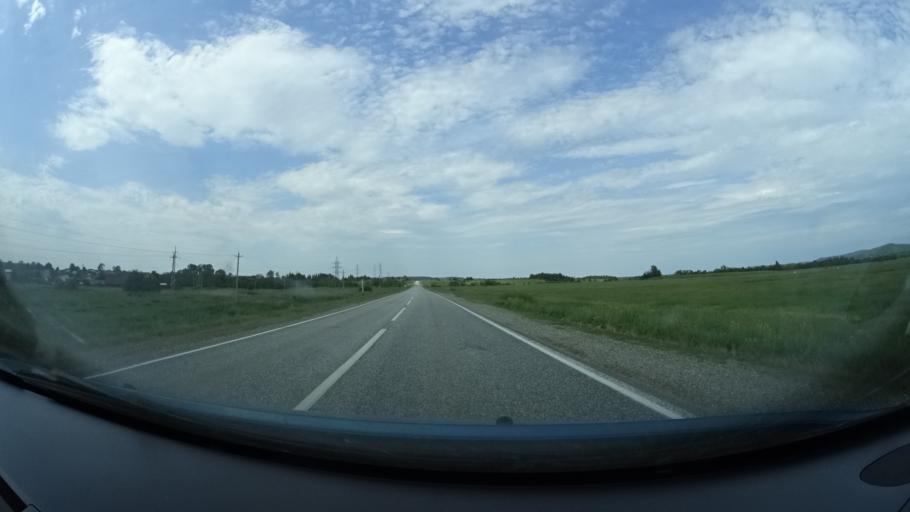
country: RU
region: Perm
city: Barda
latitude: 57.0857
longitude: 55.5408
